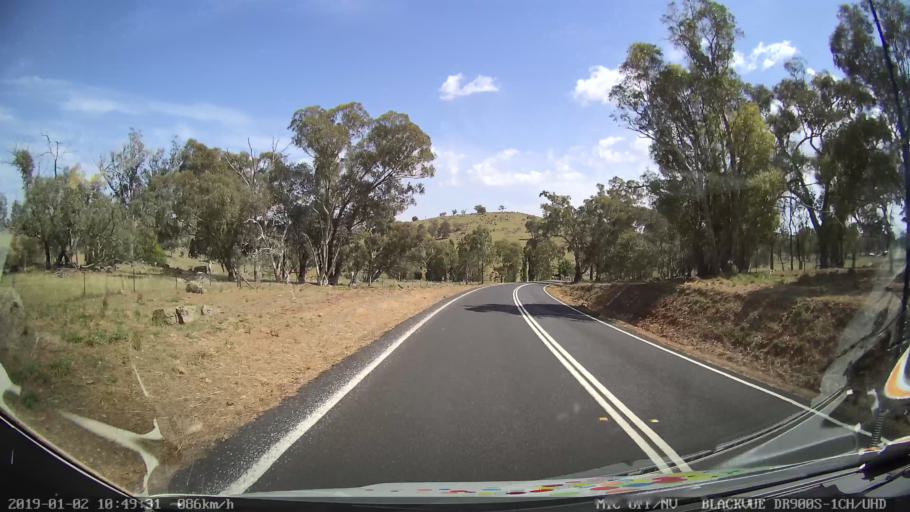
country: AU
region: New South Wales
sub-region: Cootamundra
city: Cootamundra
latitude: -34.7230
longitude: 148.2760
